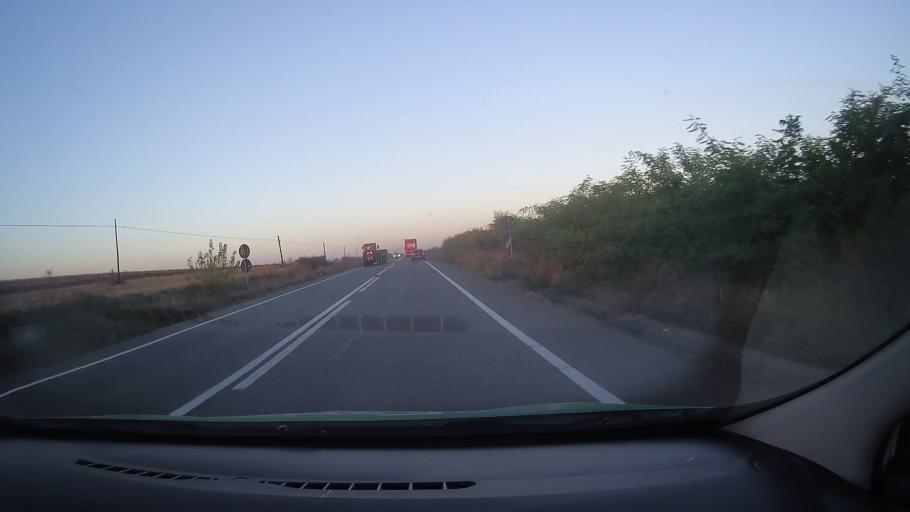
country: RO
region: Bihor
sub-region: Comuna Cherechiu
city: Cherechiu
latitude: 47.3702
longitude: 22.1296
